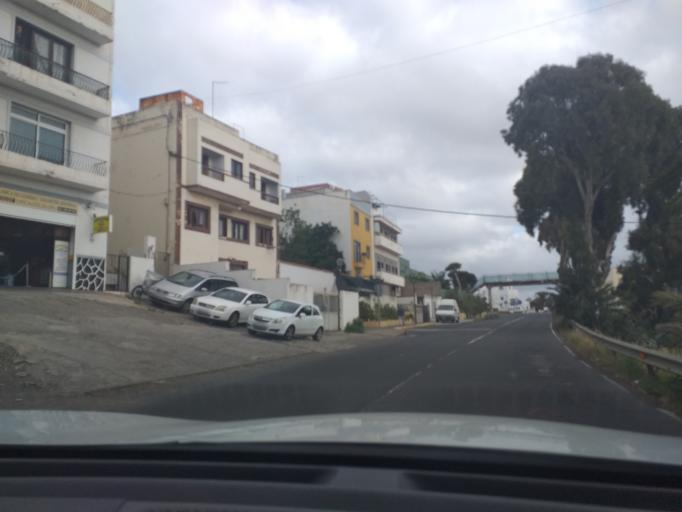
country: ES
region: Canary Islands
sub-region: Provincia de Las Palmas
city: Arucas
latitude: 28.1111
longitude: -15.5100
